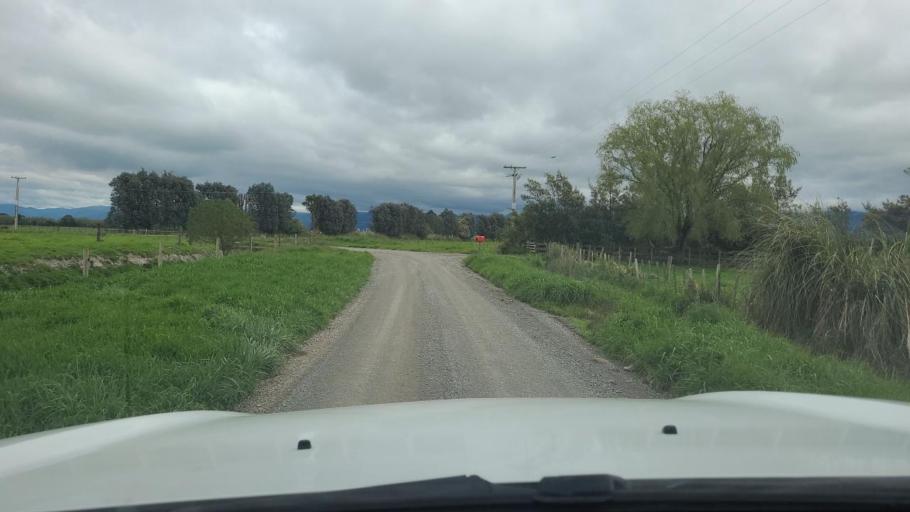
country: NZ
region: Wellington
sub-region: South Wairarapa District
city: Waipawa
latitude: -41.1431
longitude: 175.4059
